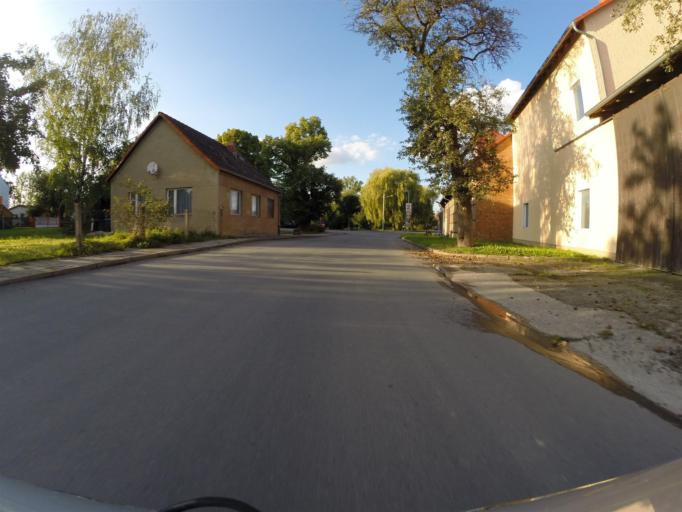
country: DE
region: Thuringia
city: Bucha
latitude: 50.8784
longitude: 11.5106
